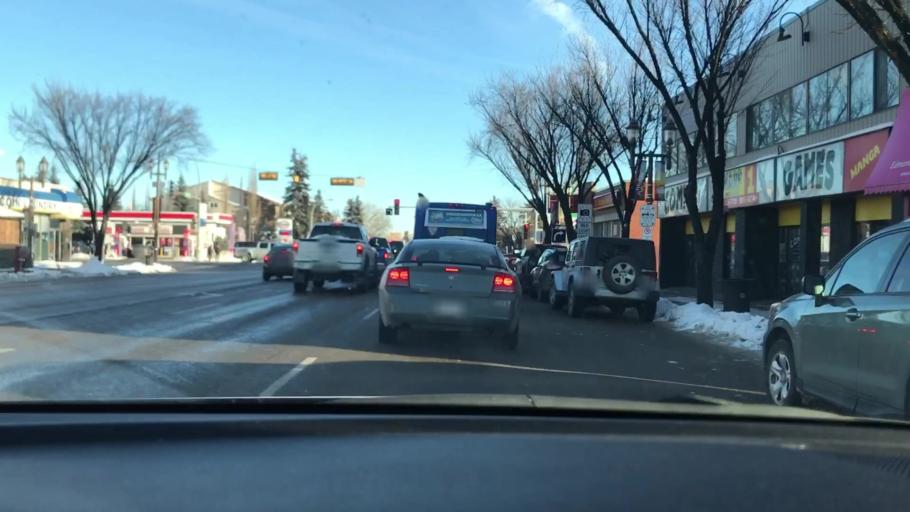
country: CA
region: Alberta
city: Edmonton
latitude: 53.5180
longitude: -113.4873
